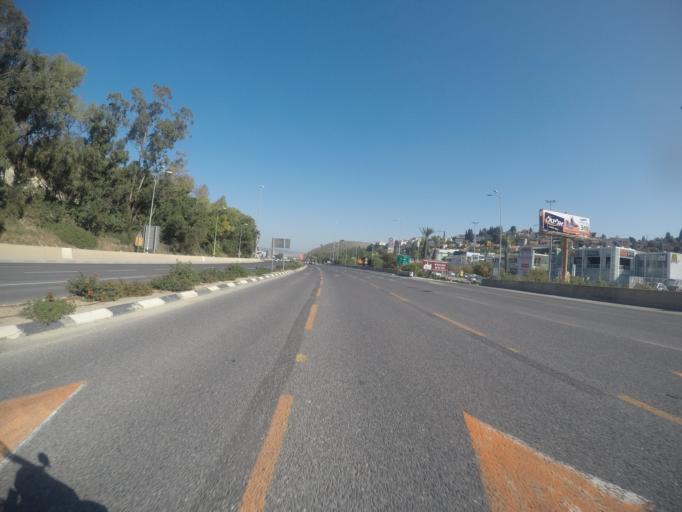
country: IL
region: Haifa
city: Daliyat el Karmil
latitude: 32.6592
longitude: 35.1034
